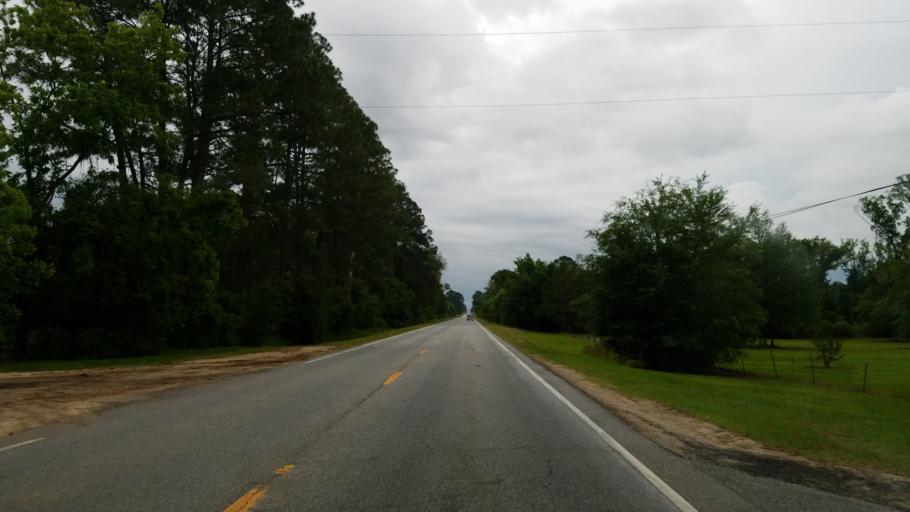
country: US
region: Georgia
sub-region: Berrien County
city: Ray City
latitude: 31.0738
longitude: -83.1861
